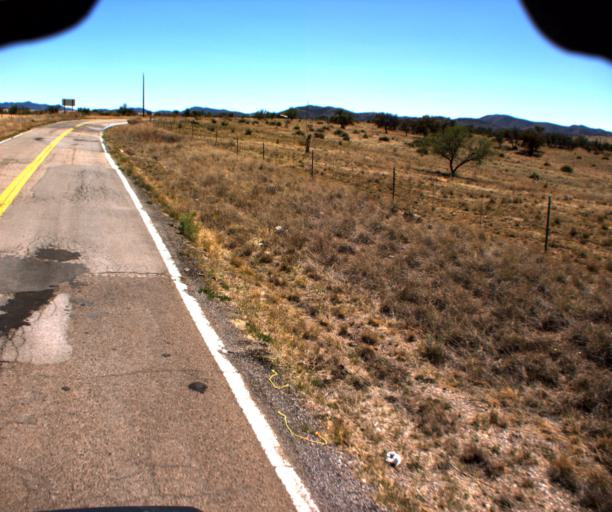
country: US
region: Arizona
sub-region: Cochise County
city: Huachuca City
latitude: 31.5997
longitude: -110.5583
